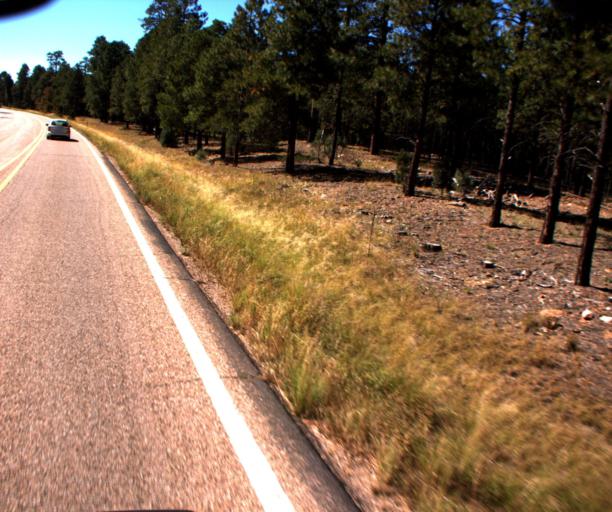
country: US
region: Arizona
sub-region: Navajo County
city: Heber-Overgaard
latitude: 34.3611
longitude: -110.6935
